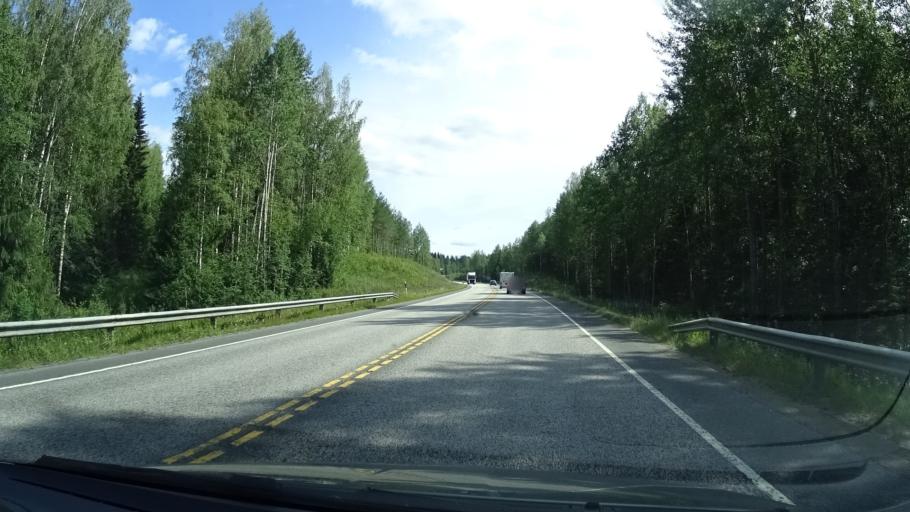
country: FI
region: Central Finland
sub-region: Jyvaeskylae
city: Jyvaeskylae
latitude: 62.2651
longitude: 25.5666
